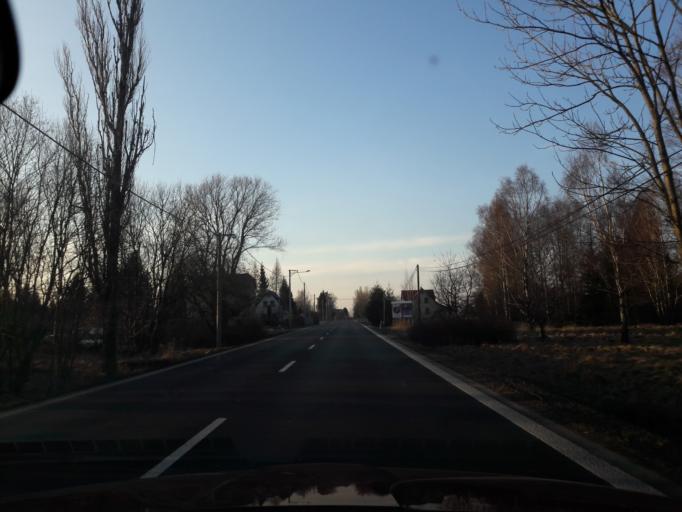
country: CZ
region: Ustecky
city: Dolni Podluzi
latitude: 50.8997
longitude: 14.5698
